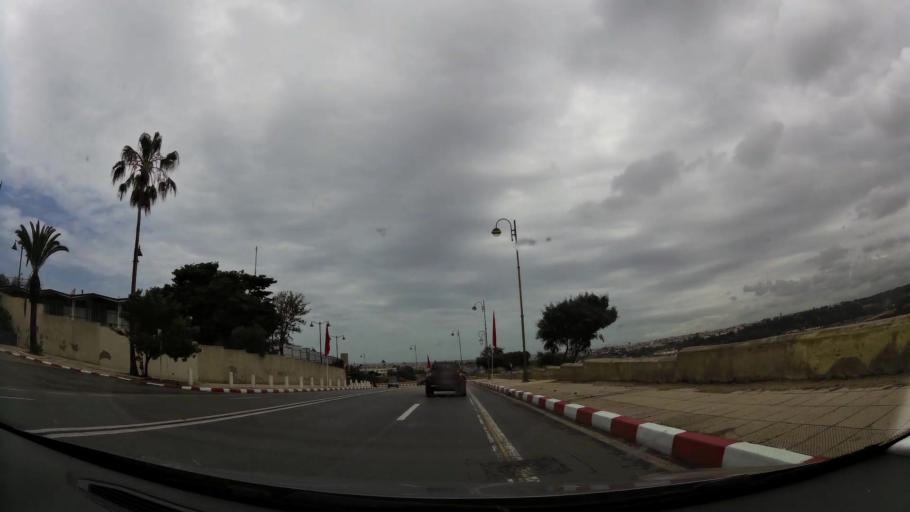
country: MA
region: Rabat-Sale-Zemmour-Zaer
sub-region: Rabat
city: Rabat
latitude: 34.0144
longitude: -6.8198
